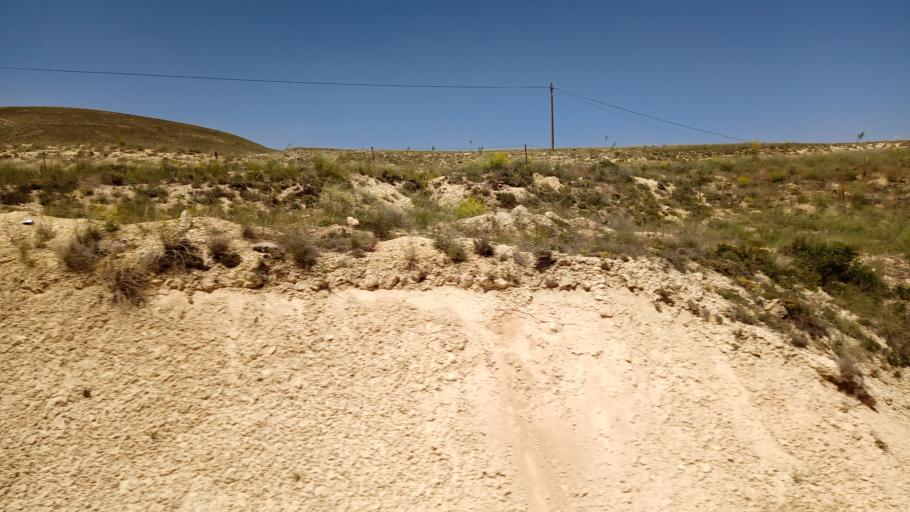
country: TR
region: Malatya
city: Darende
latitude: 38.6537
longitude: 37.4450
